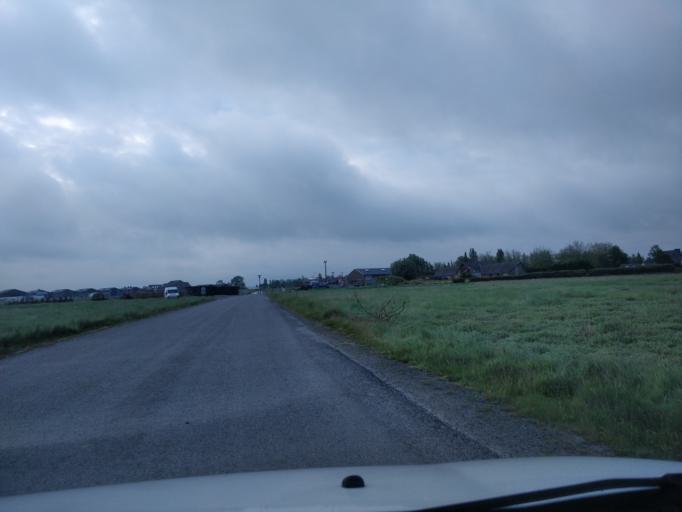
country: FR
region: Brittany
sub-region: Departement d'Ille-et-Vilaine
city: Le Vivier-sur-Mer
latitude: 48.6050
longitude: -1.7743
